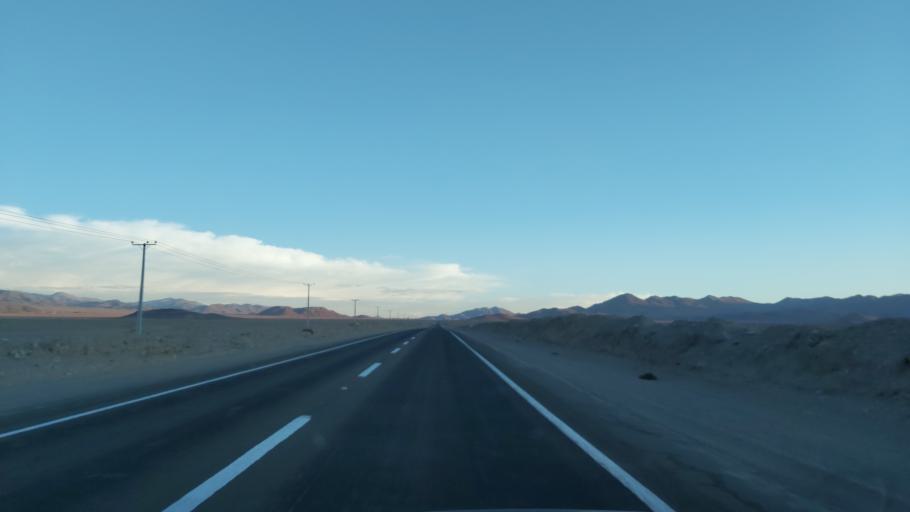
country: CL
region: Atacama
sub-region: Provincia de Chanaral
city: Diego de Almagro
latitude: -26.6956
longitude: -69.9287
